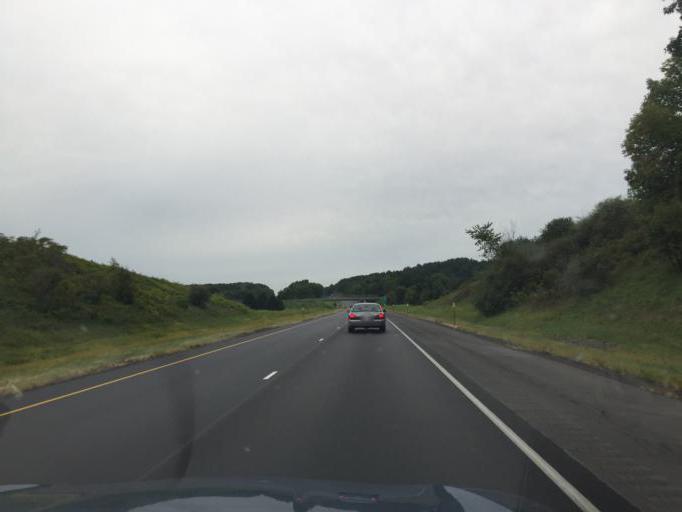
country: US
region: New York
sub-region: Rensselaer County
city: Nassau
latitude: 42.4841
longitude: -73.6427
